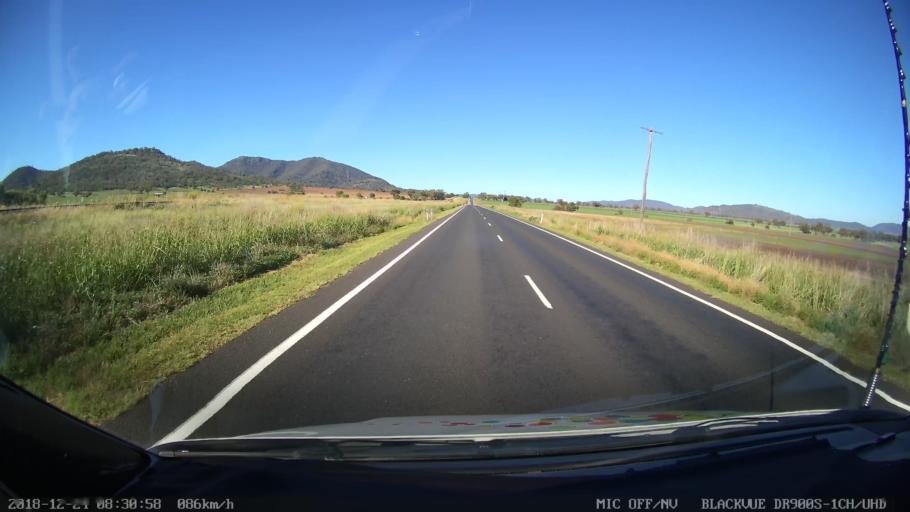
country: AU
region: New South Wales
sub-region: Tamworth Municipality
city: Phillip
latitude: -31.2705
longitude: 150.7180
